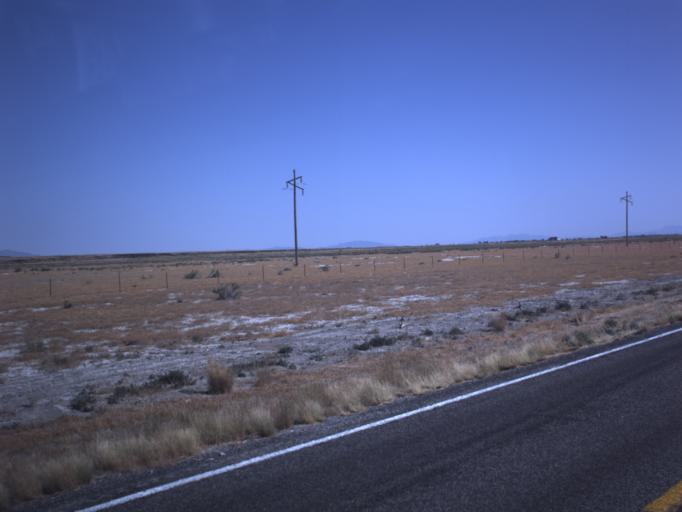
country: US
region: Utah
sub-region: Millard County
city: Delta
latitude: 39.1934
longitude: -112.6922
